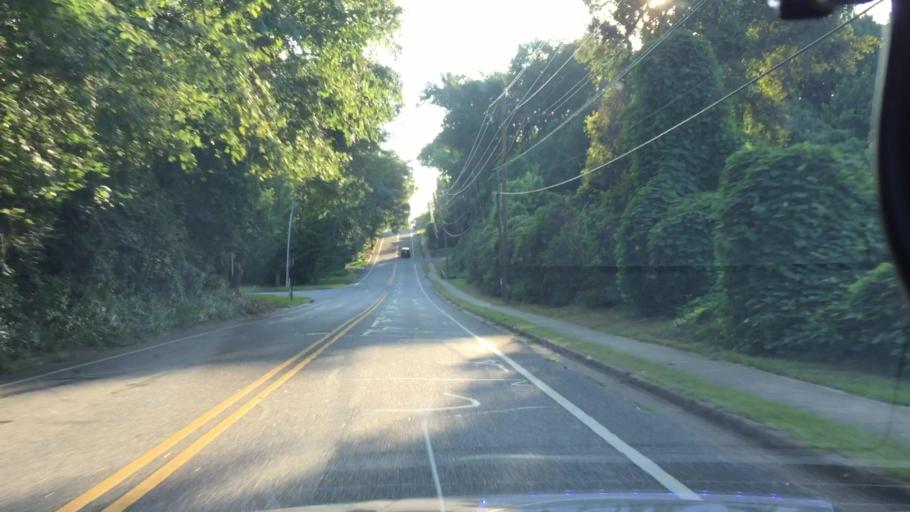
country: US
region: Alabama
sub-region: Lee County
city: Auburn
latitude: 32.6044
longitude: -85.4700
